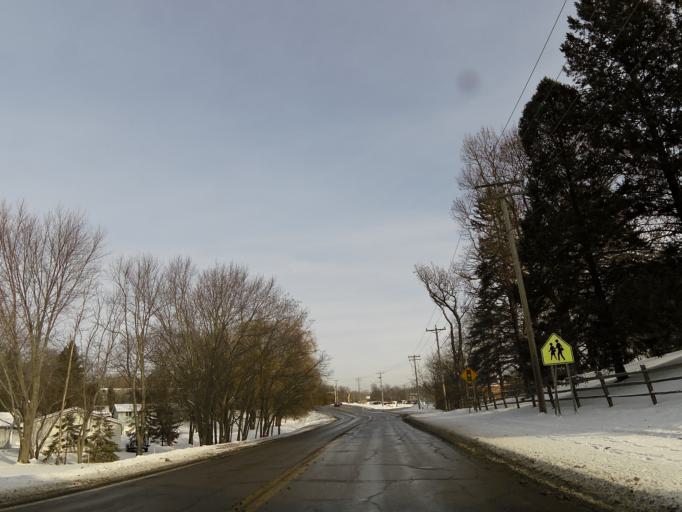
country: US
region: Minnesota
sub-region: Hennepin County
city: Minnetonka
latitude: 44.8993
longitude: -93.5126
